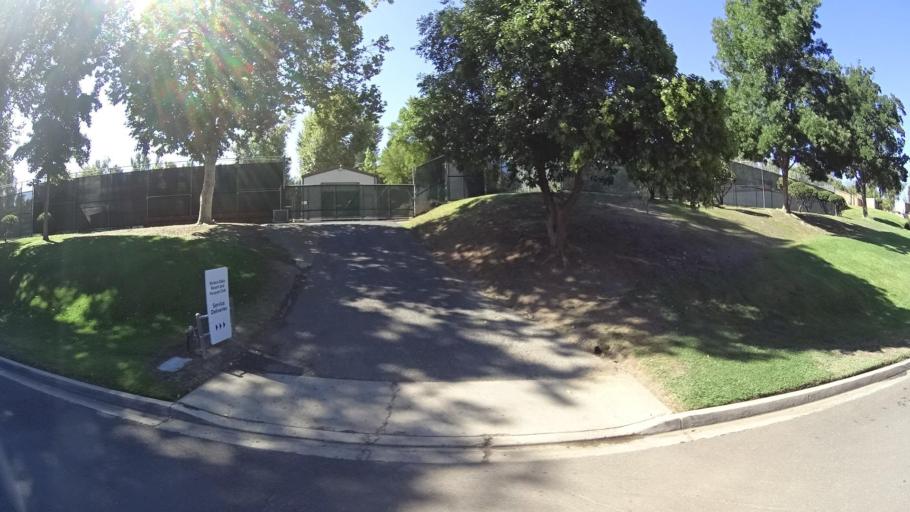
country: US
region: California
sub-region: San Diego County
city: San Diego Country Estates
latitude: 33.0039
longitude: -116.7795
